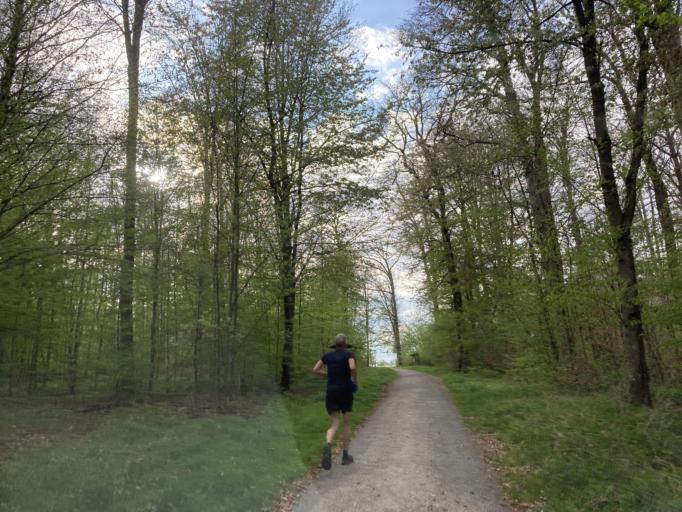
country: DE
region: Baden-Wuerttemberg
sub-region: Tuebingen Region
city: Wannweil
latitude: 48.5166
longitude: 9.1372
